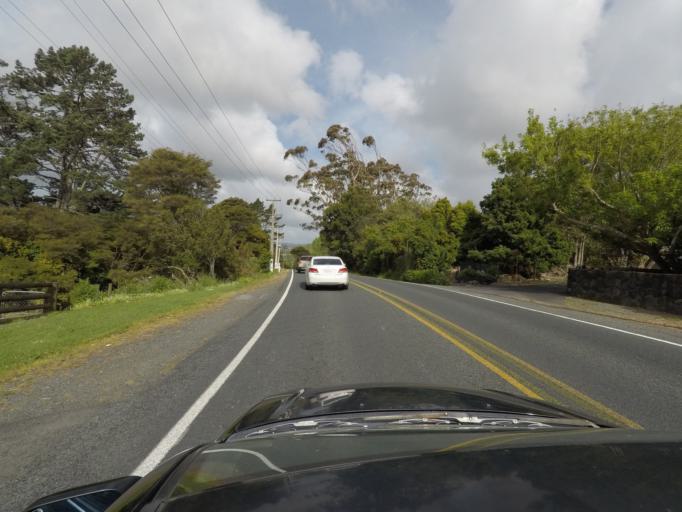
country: NZ
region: Auckland
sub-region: Auckland
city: Pakuranga
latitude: -36.9441
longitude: 174.9507
